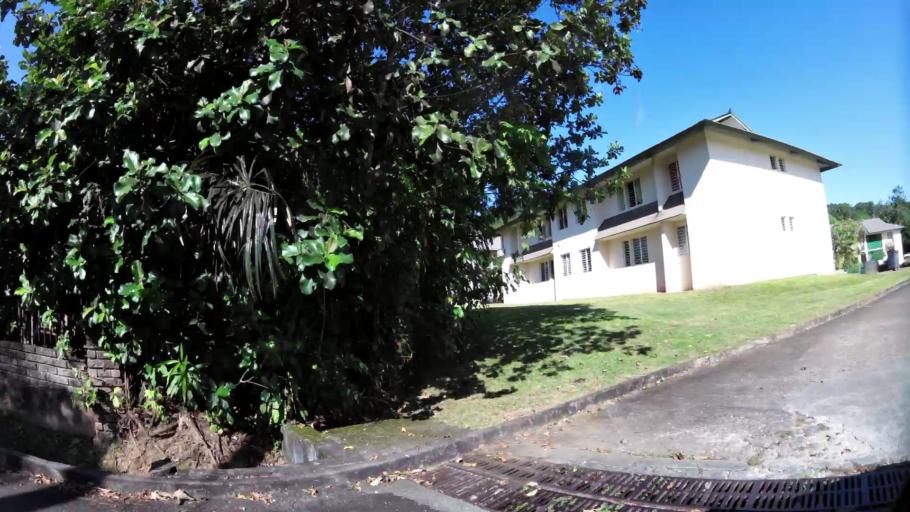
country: GF
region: Guyane
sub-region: Guyane
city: Remire-Montjoly
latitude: 4.8807
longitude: -52.2783
